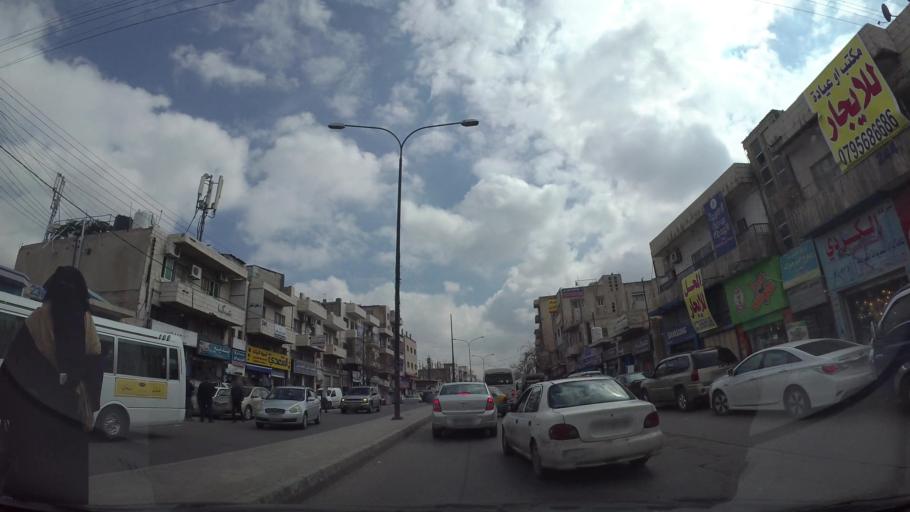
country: JO
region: Amman
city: Al Quwaysimah
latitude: 31.9282
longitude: 35.9374
